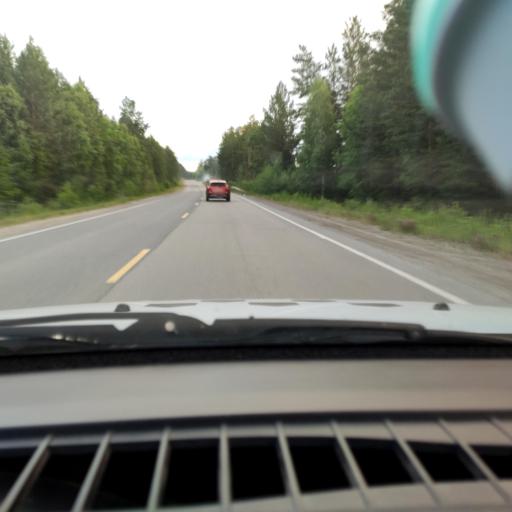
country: RU
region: Chelyabinsk
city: Kyshtym
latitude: 55.6969
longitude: 60.5027
